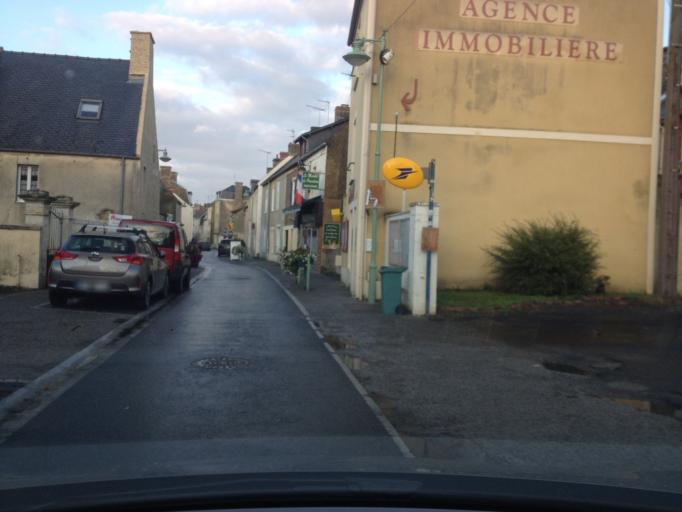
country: FR
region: Lower Normandy
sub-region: Departement du Calvados
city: Grandcamp-Maisy
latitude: 49.3879
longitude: -1.0450
